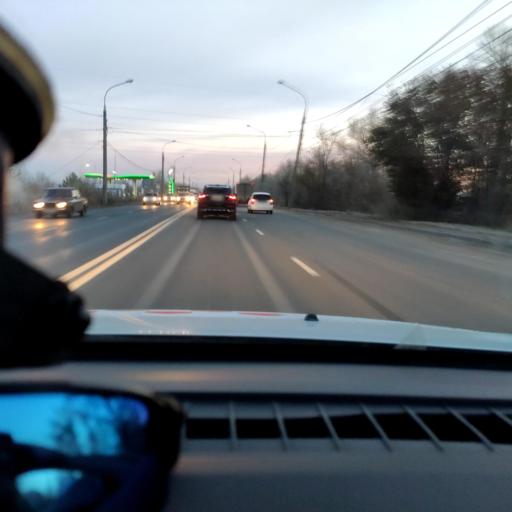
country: RU
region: Samara
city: Samara
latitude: 53.1439
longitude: 50.1815
